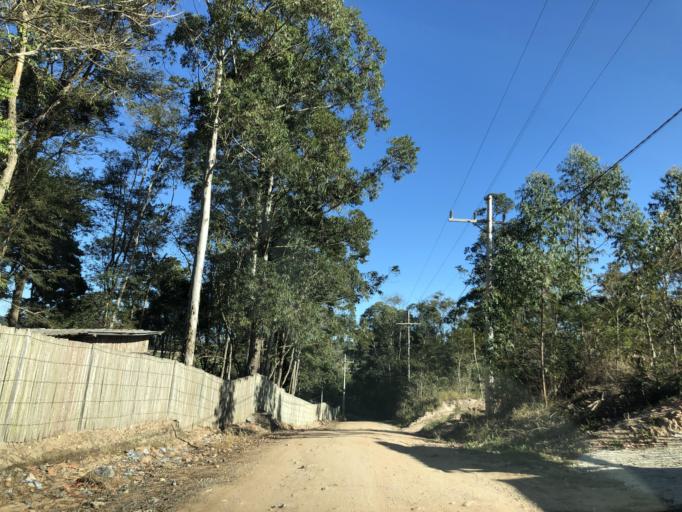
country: BR
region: Sao Paulo
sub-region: Pilar Do Sul
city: Pilar do Sul
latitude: -23.8176
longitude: -47.6309
